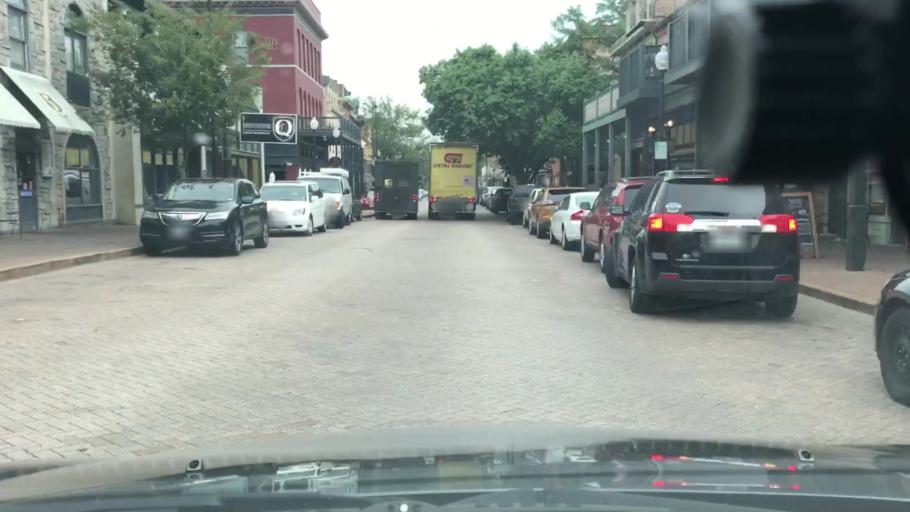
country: US
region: Missouri
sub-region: Saint Charles County
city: Saint Charles
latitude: 38.7818
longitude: -90.4810
